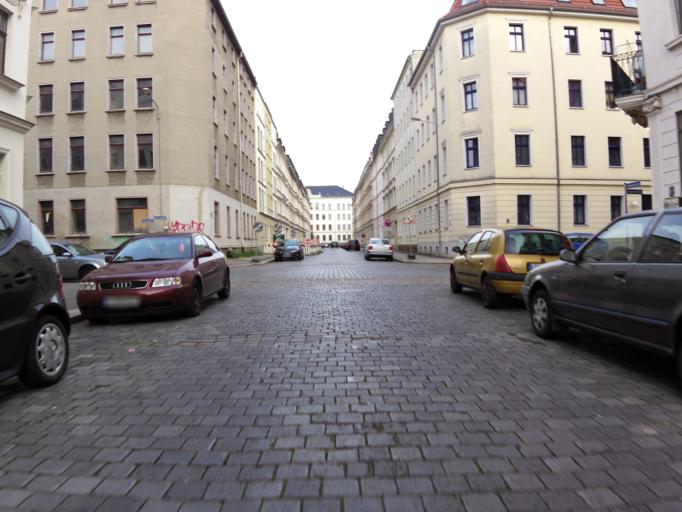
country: DE
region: Saxony
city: Leipzig
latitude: 51.3339
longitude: 12.4100
